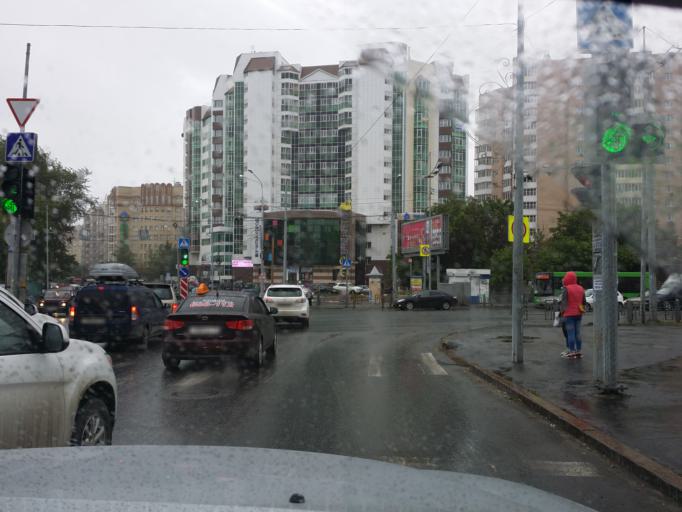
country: RU
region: Tjumen
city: Tyumen
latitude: 57.1462
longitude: 65.5443
